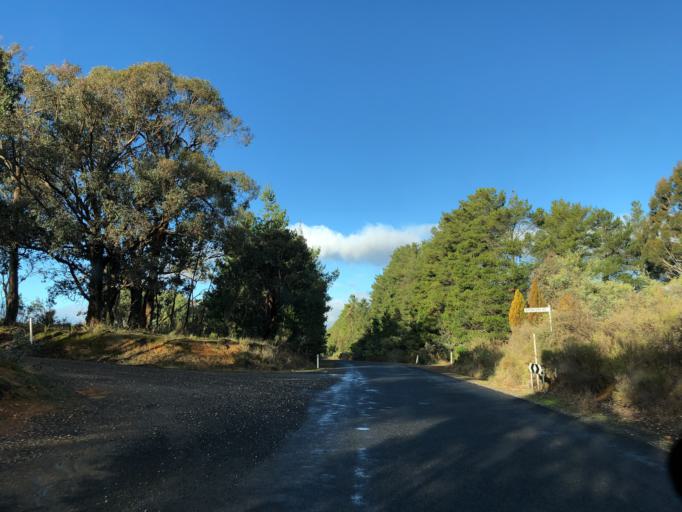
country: AU
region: Victoria
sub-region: Mount Alexander
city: Castlemaine
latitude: -37.2085
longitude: 144.2944
